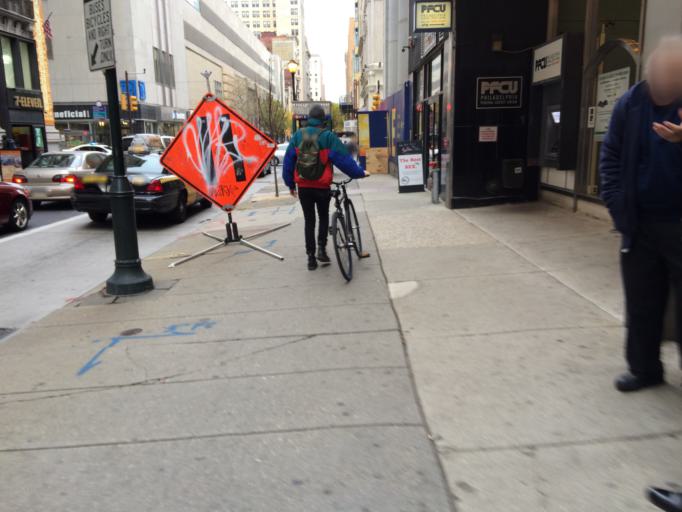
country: US
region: Pennsylvania
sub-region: Philadelphia County
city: Philadelphia
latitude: 39.9504
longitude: -75.1608
